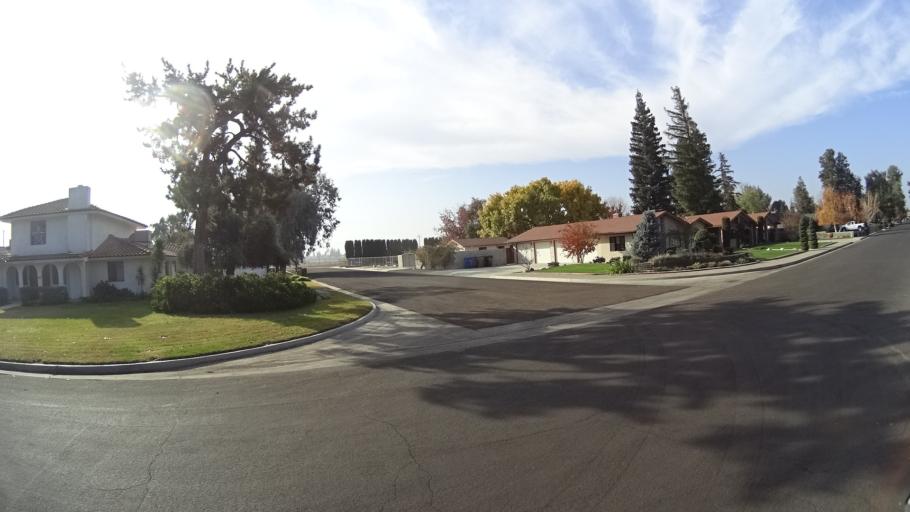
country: US
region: California
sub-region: Kern County
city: Rosedale
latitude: 35.3671
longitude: -119.1499
